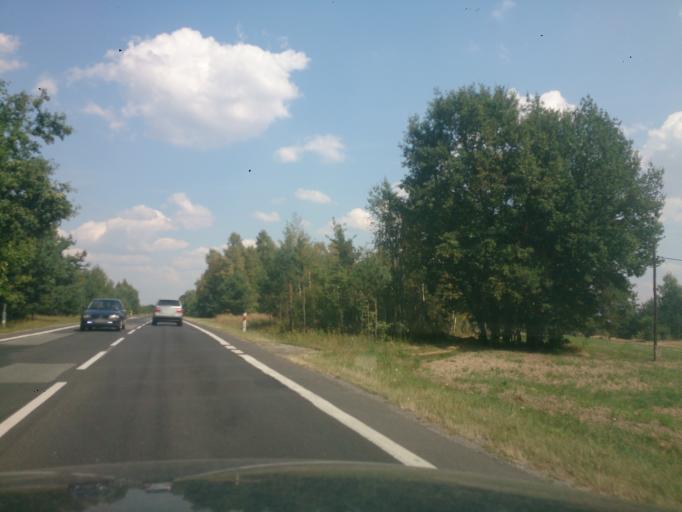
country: PL
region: Subcarpathian Voivodeship
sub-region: Powiat kolbuszowski
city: Majdan Krolewski
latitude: 50.3601
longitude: 21.7271
